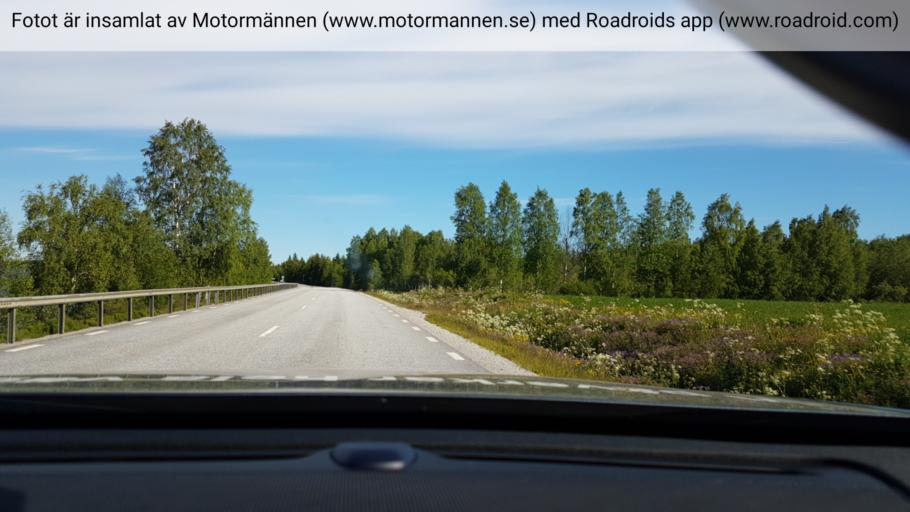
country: SE
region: Vaesterbotten
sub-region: Vindelns Kommun
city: Vindeln
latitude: 64.1806
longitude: 19.4769
